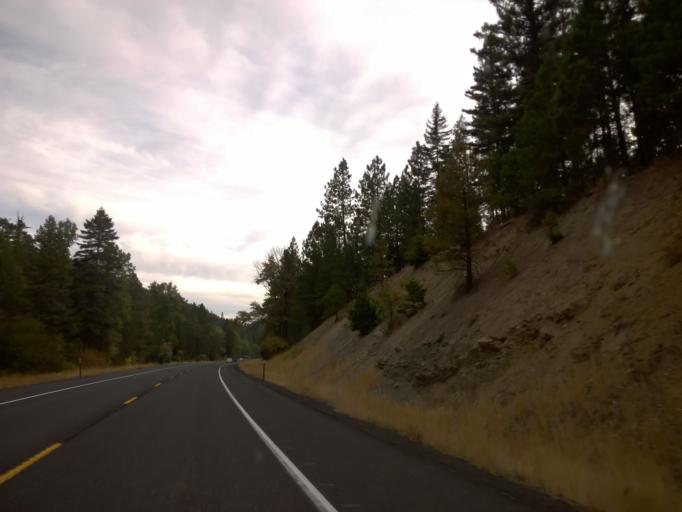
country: US
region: Washington
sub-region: Kittitas County
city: Cle Elum
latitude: 47.3111
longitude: -120.6935
